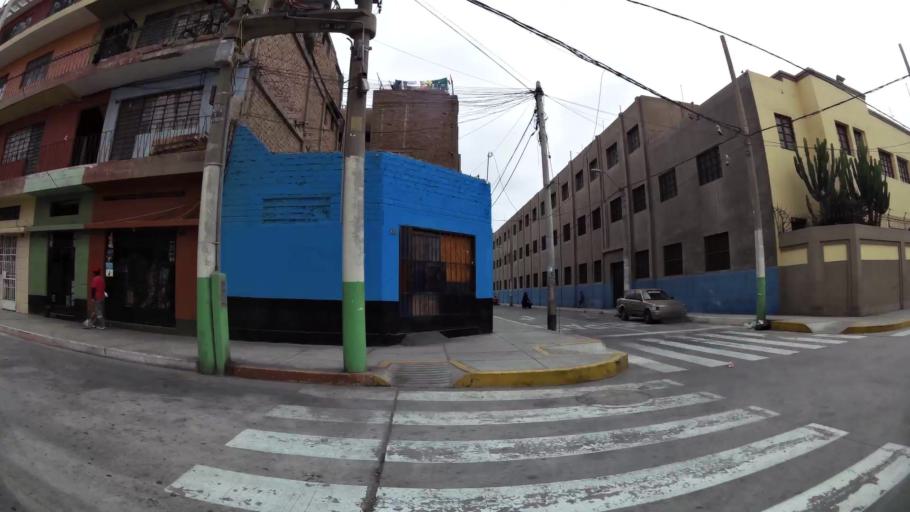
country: PE
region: Callao
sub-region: Callao
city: Callao
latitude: -12.0556
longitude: -77.1412
